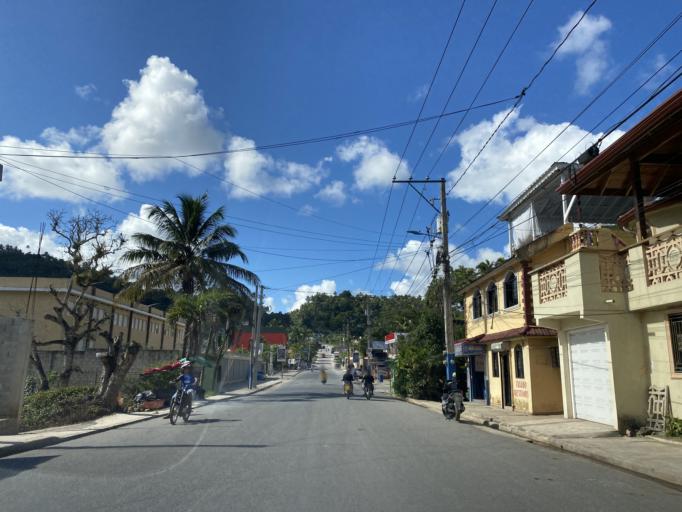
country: DO
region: Samana
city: Samana
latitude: 19.2057
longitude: -69.3462
